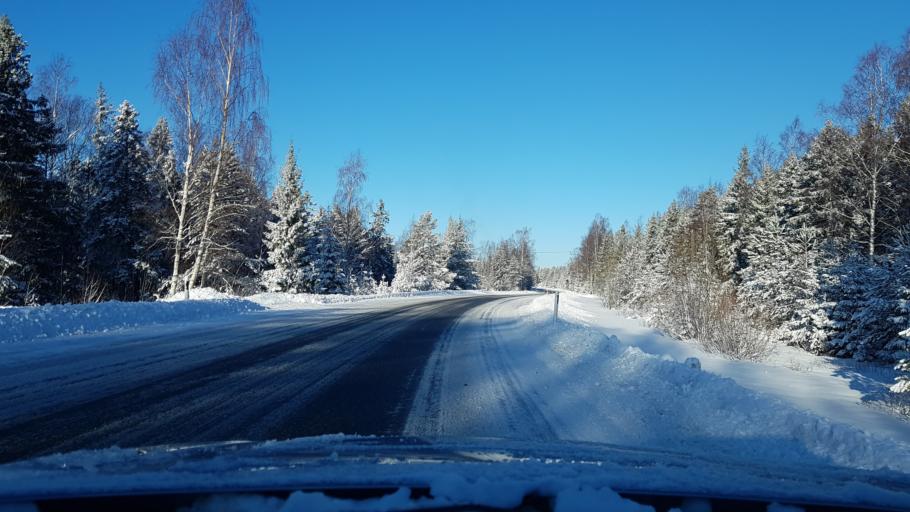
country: EE
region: Hiiumaa
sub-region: Kaerdla linn
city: Kardla
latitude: 58.9781
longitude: 22.8124
